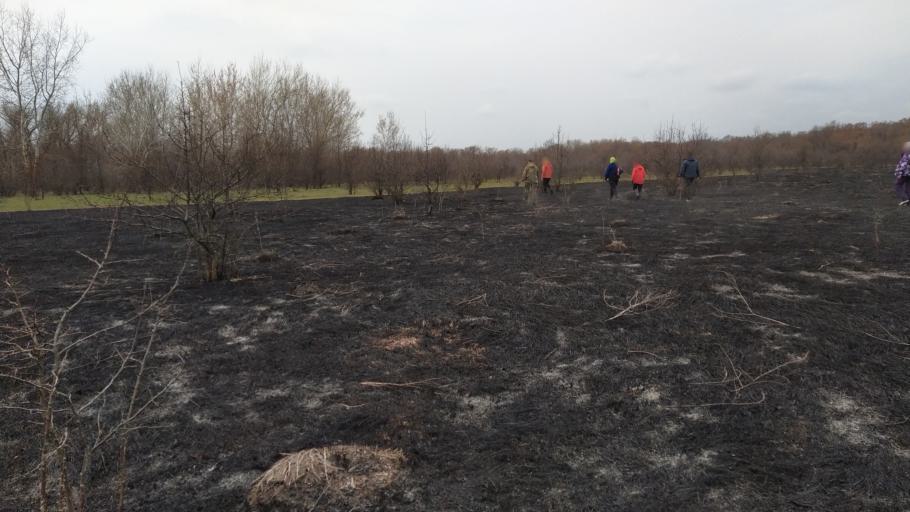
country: RU
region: Rostov
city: Semikarakorsk
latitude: 47.5413
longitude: 40.6832
